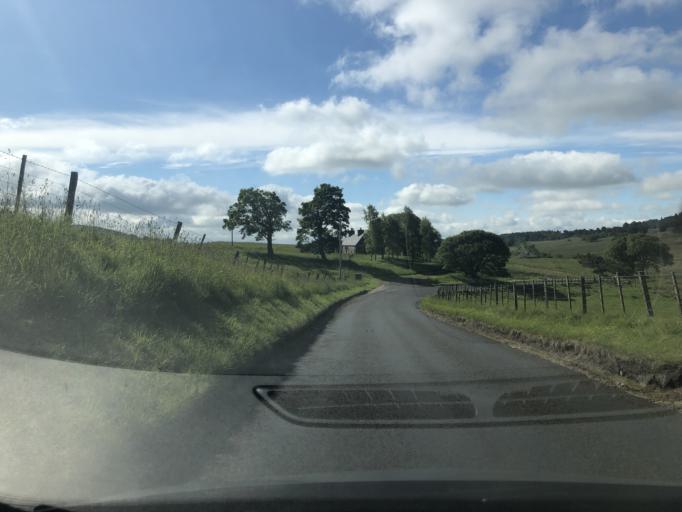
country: GB
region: Scotland
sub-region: Angus
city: Kirriemuir
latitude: 56.7572
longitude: -3.0166
